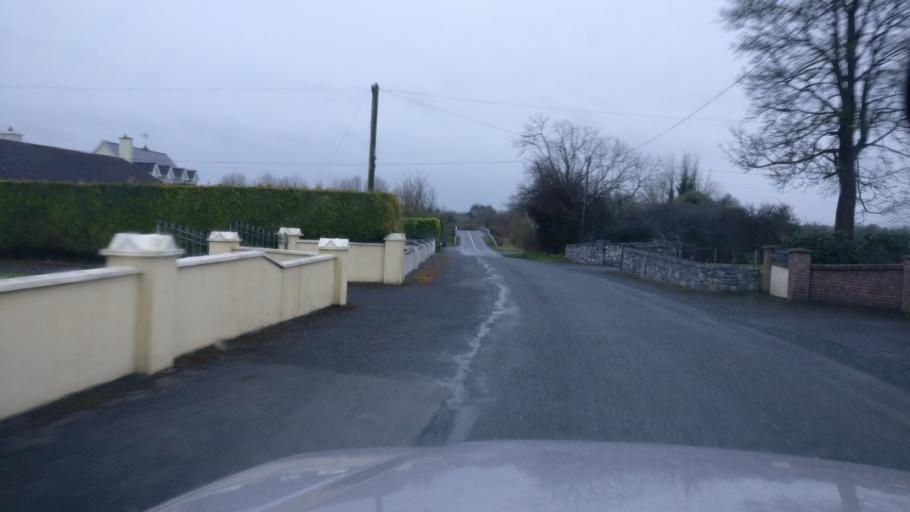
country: IE
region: Connaught
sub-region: County Galway
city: Ballinasloe
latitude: 53.3091
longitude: -8.2796
